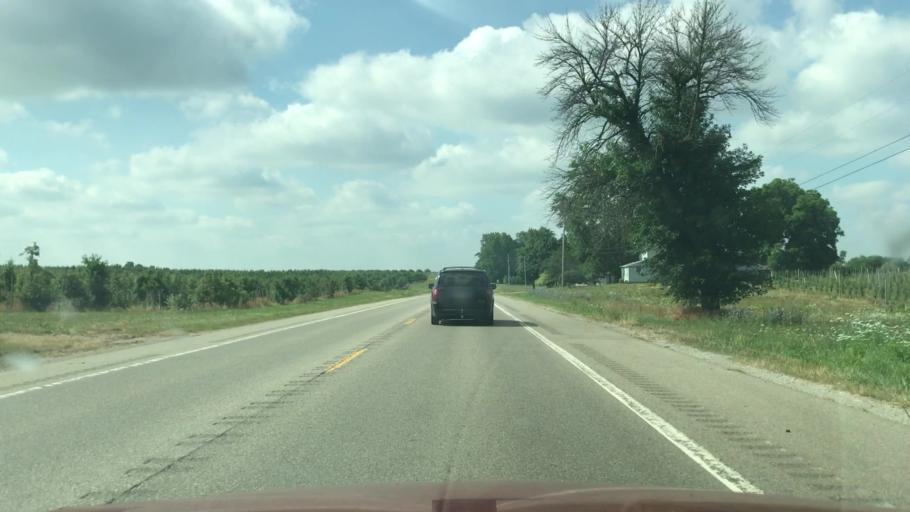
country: US
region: Michigan
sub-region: Kent County
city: Kent City
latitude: 43.2456
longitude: -85.8105
